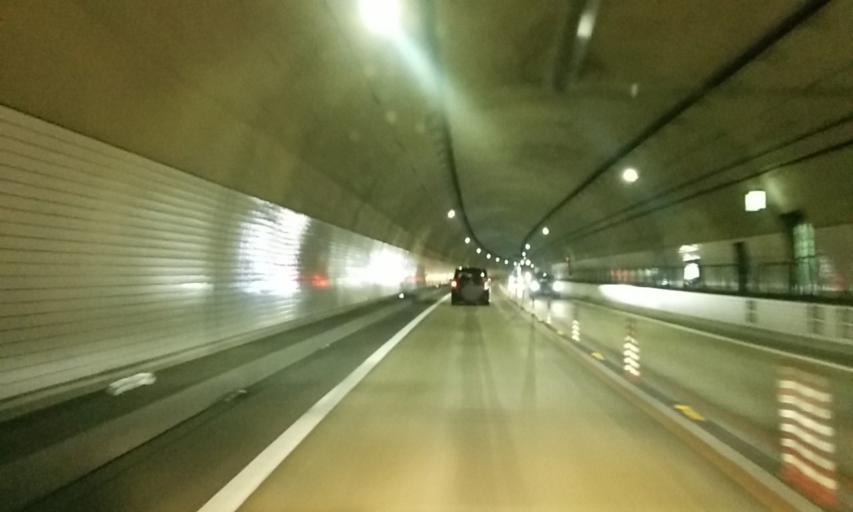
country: JP
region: Kyoto
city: Miyazu
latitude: 35.5538
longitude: 135.1303
